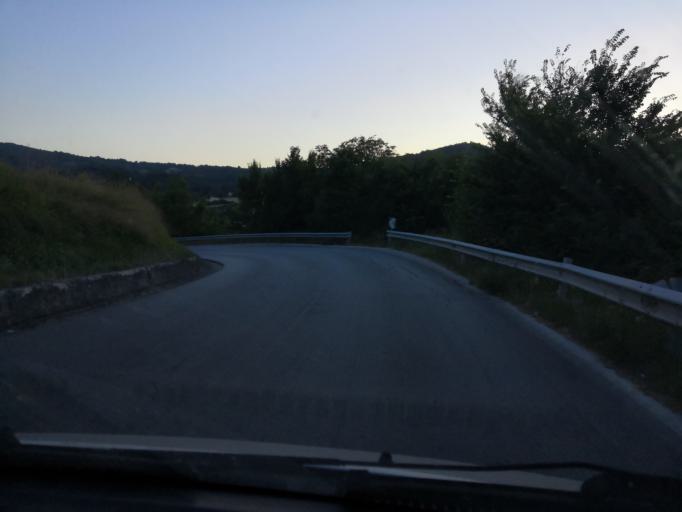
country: IT
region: Molise
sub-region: Provincia di Campobasso
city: Jelsi
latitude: 41.5151
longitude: 14.7933
